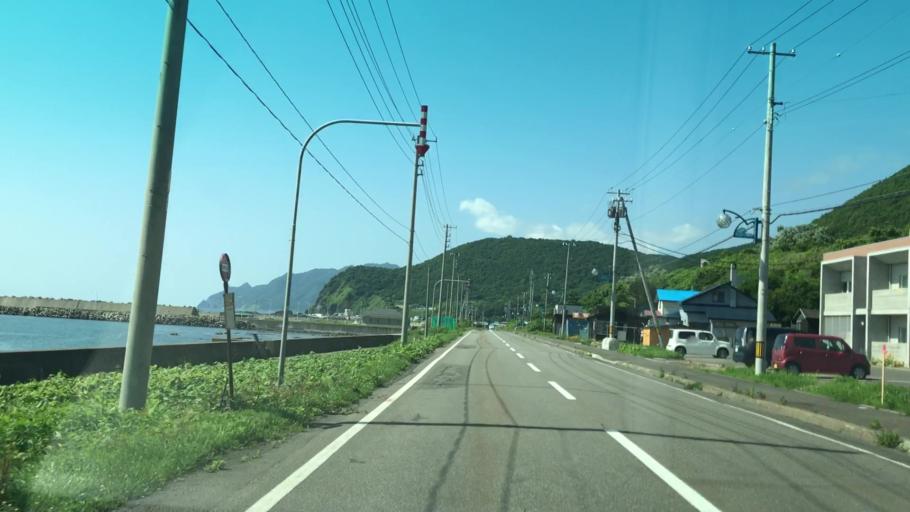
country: JP
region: Hokkaido
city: Iwanai
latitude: 43.0957
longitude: 140.4628
